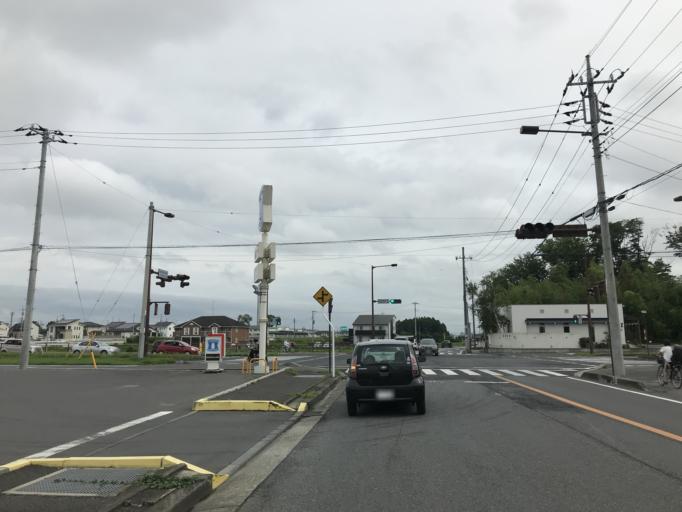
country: JP
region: Ibaraki
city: Mito-shi
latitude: 36.3365
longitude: 140.4589
